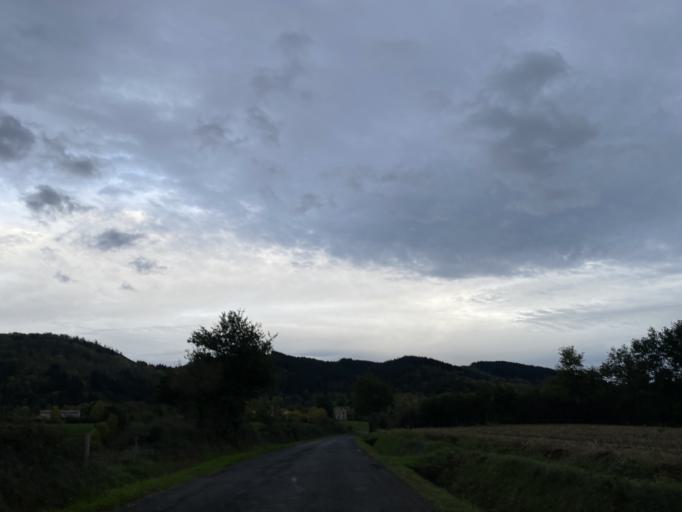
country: FR
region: Auvergne
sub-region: Departement du Puy-de-Dome
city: Thiers
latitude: 45.8398
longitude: 3.5402
